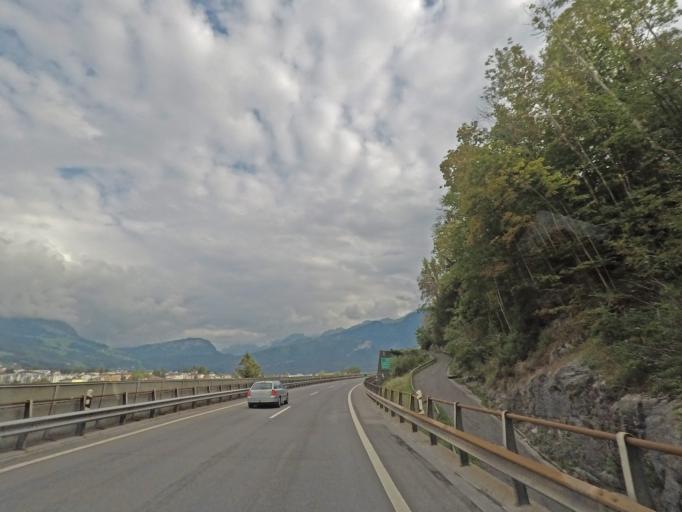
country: CH
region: Schwyz
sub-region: Bezirk Schwyz
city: Ibach
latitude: 47.0277
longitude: 8.6282
